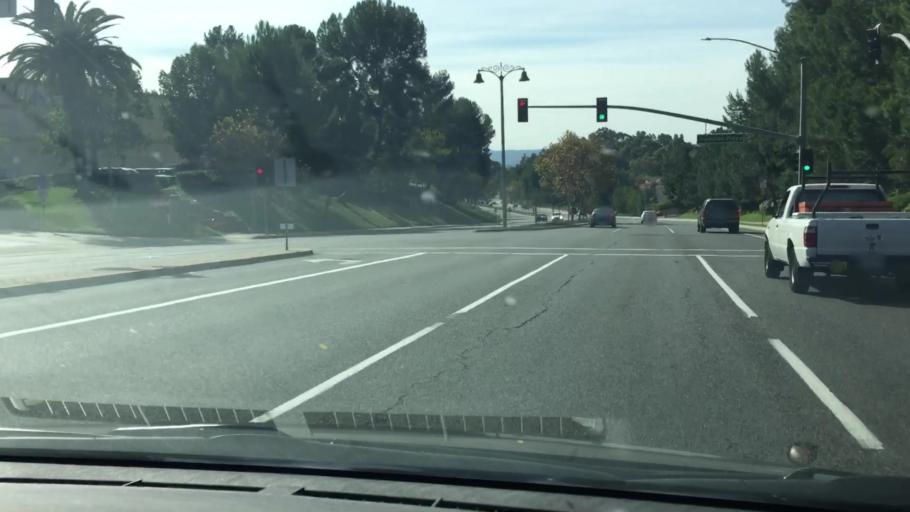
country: US
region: California
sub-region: Orange County
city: Rancho Santa Margarita
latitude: 33.6285
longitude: -117.6358
